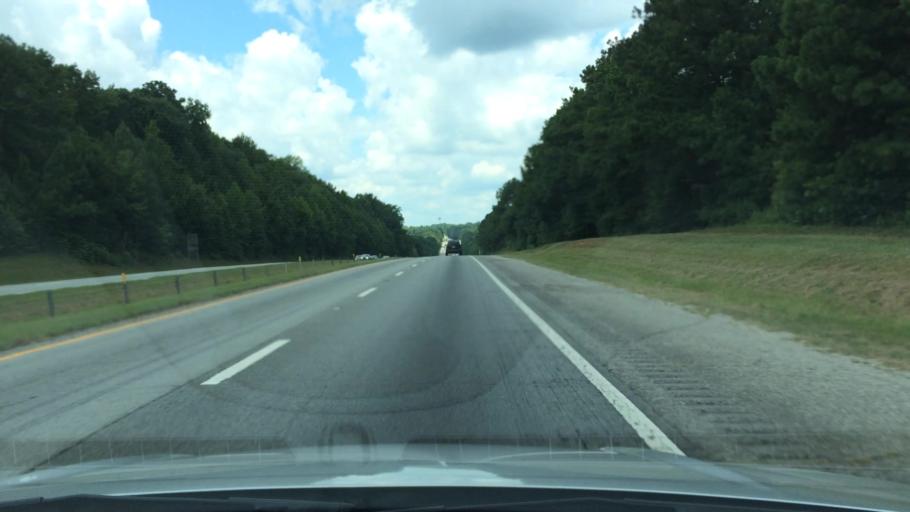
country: US
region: South Carolina
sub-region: Lexington County
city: Chapin
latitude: 34.2270
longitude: -81.4296
